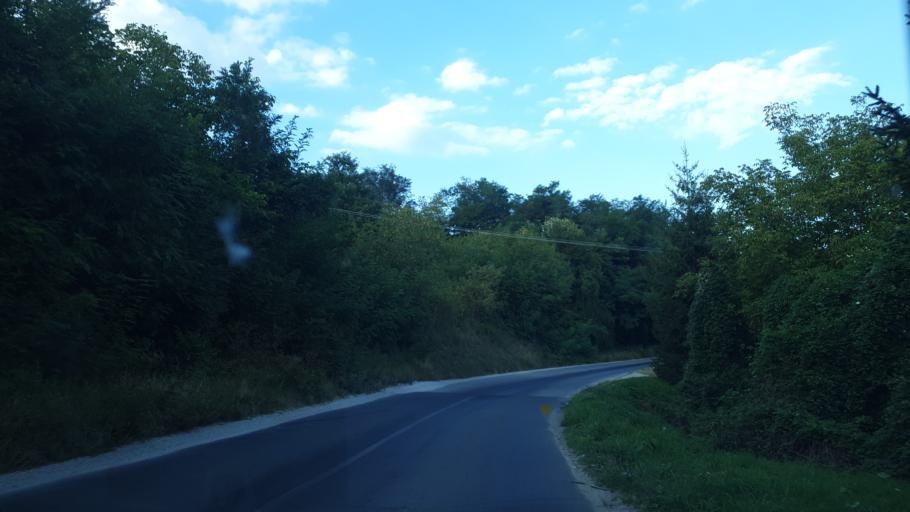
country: RS
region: Central Serbia
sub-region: Zlatiborski Okrug
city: Uzice
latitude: 43.8613
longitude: 19.8804
